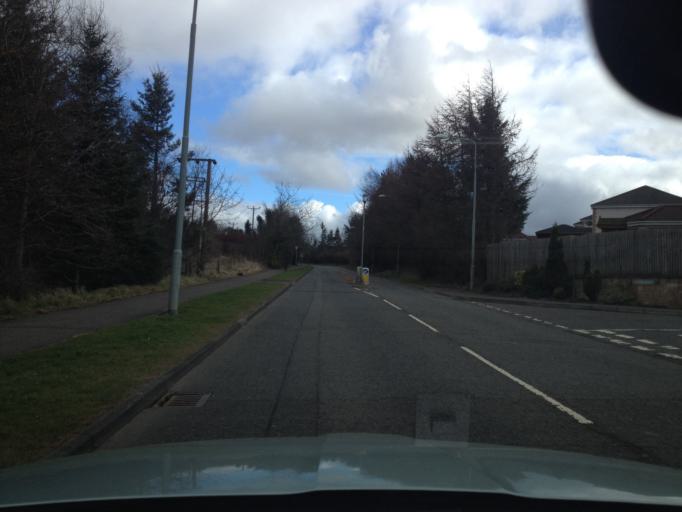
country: GB
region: Scotland
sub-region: West Lothian
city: Livingston
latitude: 55.8587
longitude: -3.5166
